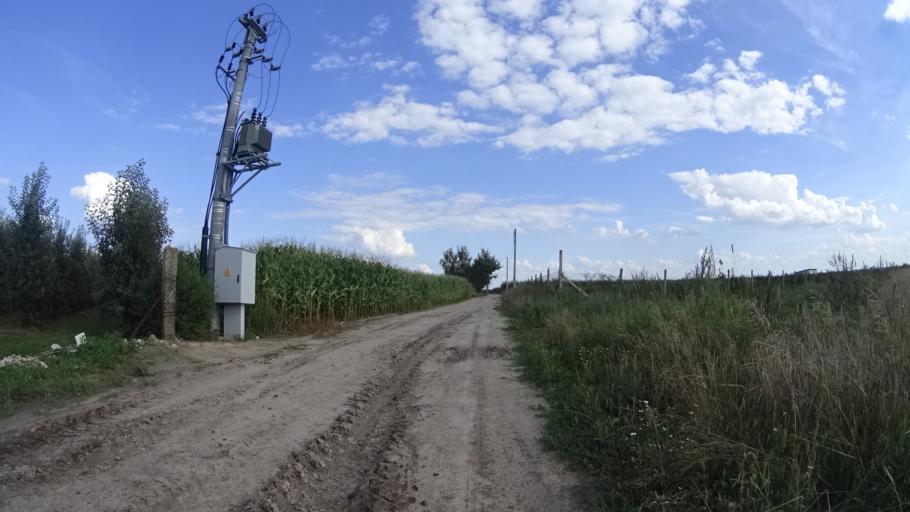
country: PL
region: Masovian Voivodeship
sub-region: Powiat bialobrzeski
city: Wysmierzyce
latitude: 51.6699
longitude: 20.8043
